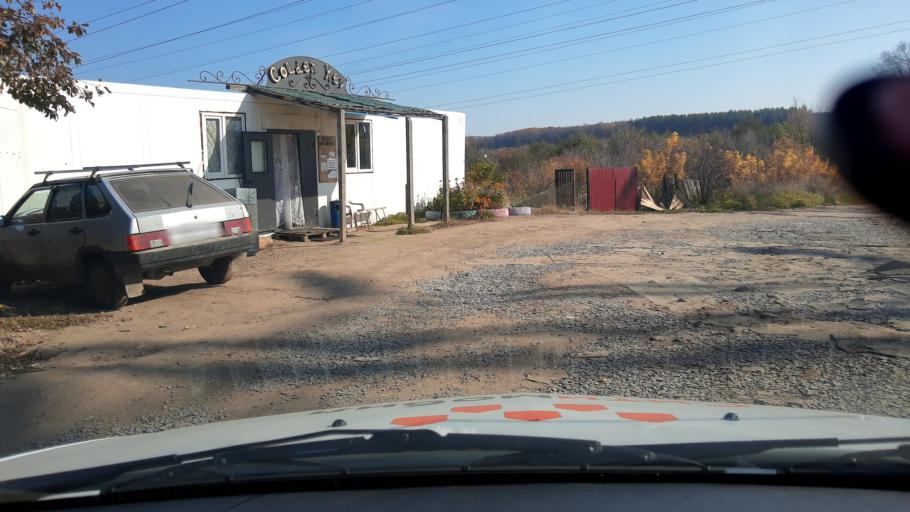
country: RU
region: Bashkortostan
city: Ufa
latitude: 54.8647
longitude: 56.1295
